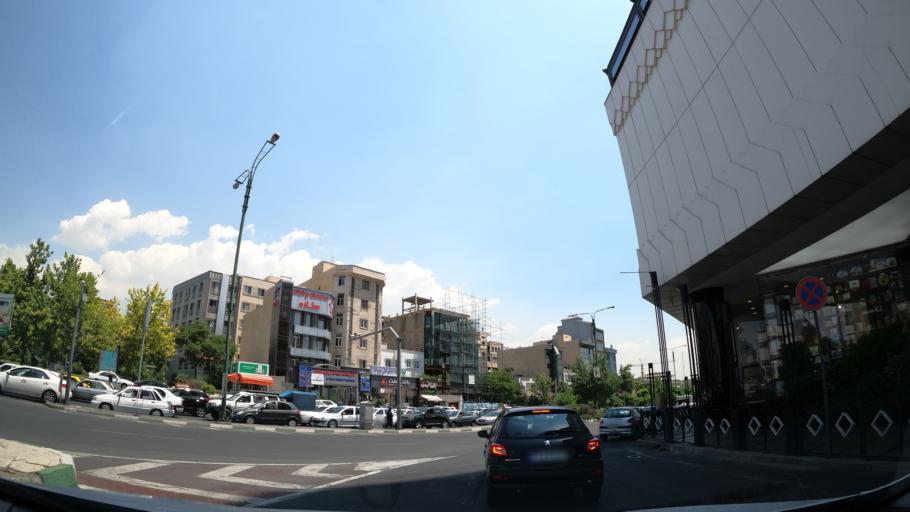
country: IR
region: Tehran
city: Tajrish
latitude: 35.7706
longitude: 51.3790
